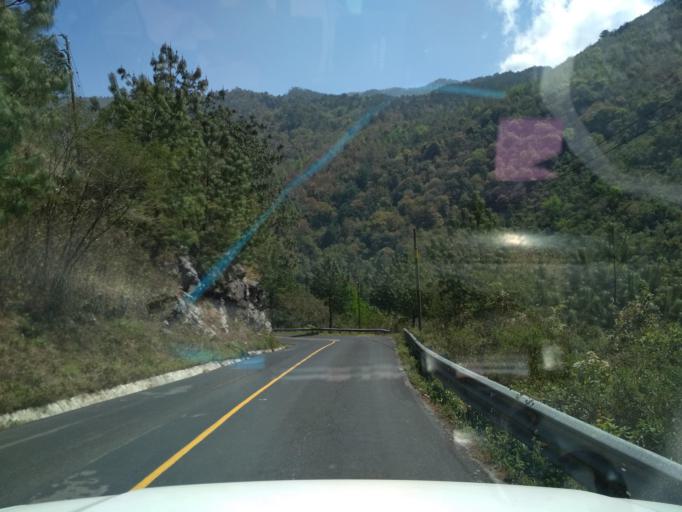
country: MX
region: Veracruz
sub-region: Tlilapan
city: Tonalixco
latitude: 18.7637
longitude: -97.0817
